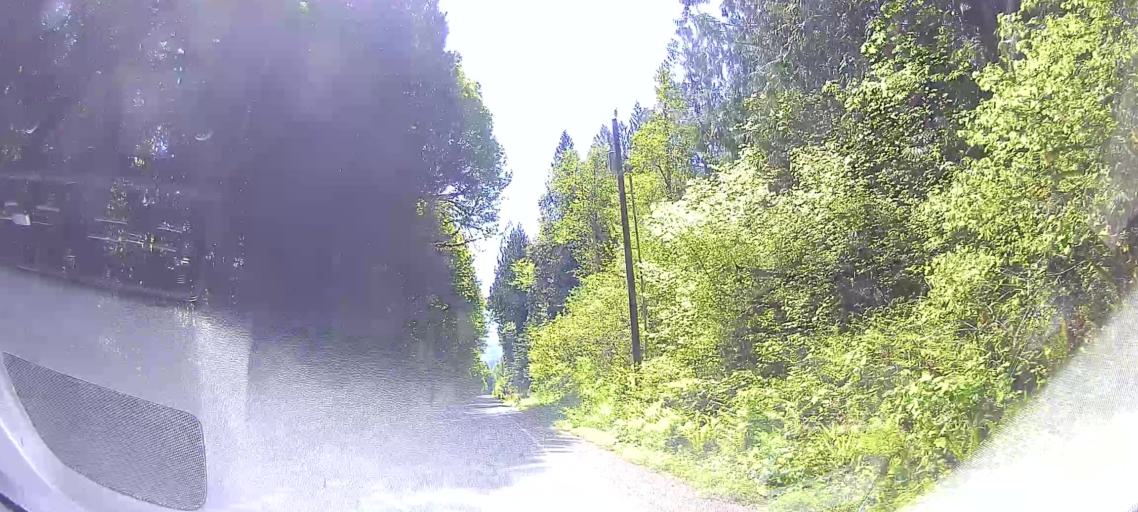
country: US
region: Washington
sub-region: Snohomish County
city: Darrington
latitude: 48.4949
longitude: -121.6589
